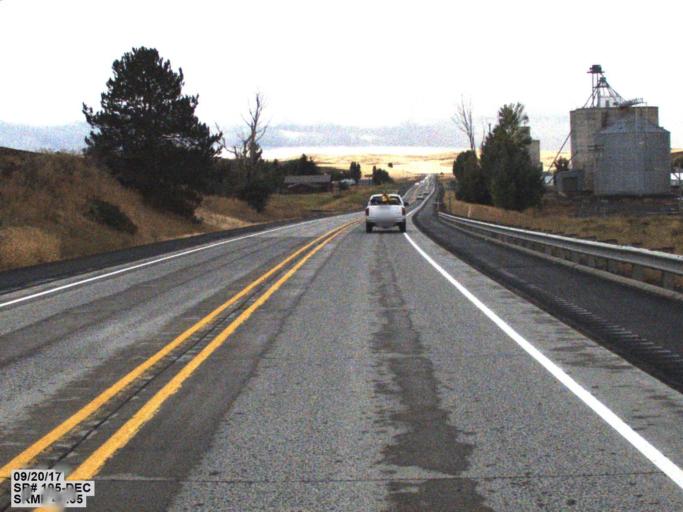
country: US
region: Washington
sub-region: Whitman County
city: Colfax
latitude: 47.0111
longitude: -117.3542
